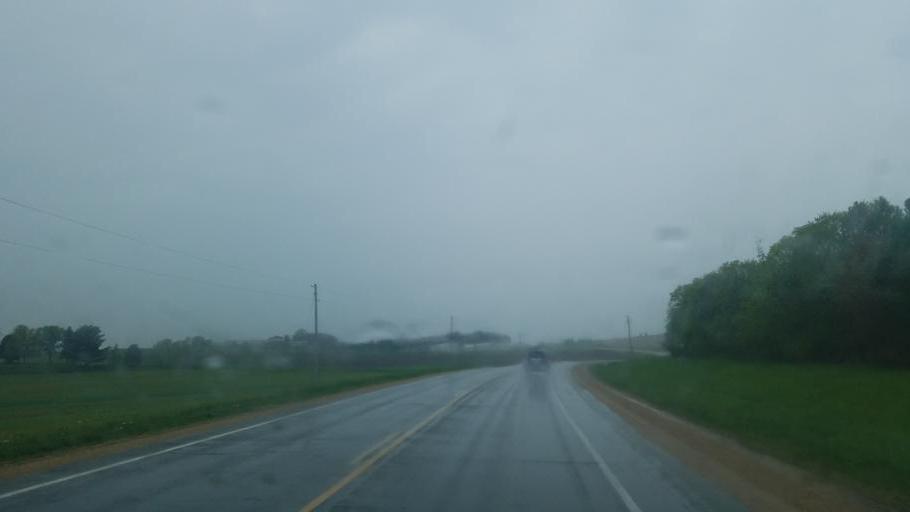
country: US
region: Wisconsin
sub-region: Sauk County
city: Reedsburg
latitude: 43.5628
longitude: -90.0788
